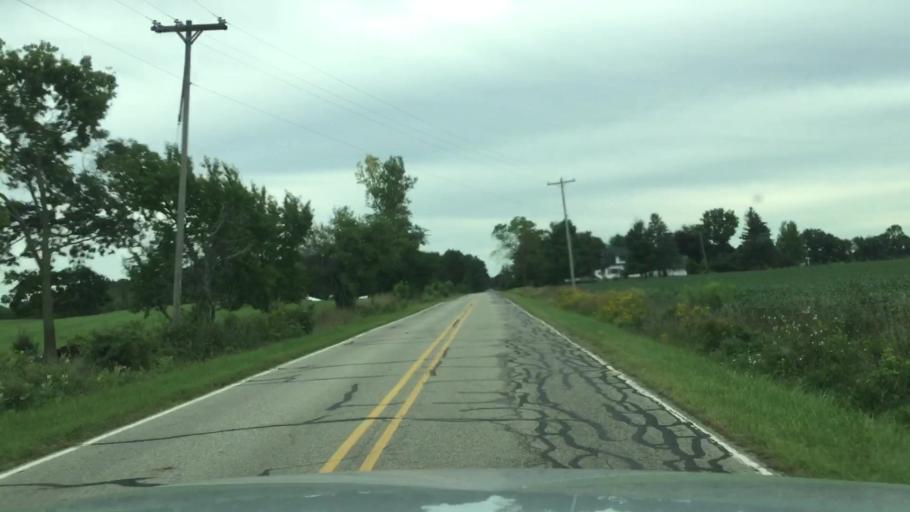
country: US
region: Michigan
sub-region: Shiawassee County
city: Corunna
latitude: 42.9259
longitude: -84.0770
